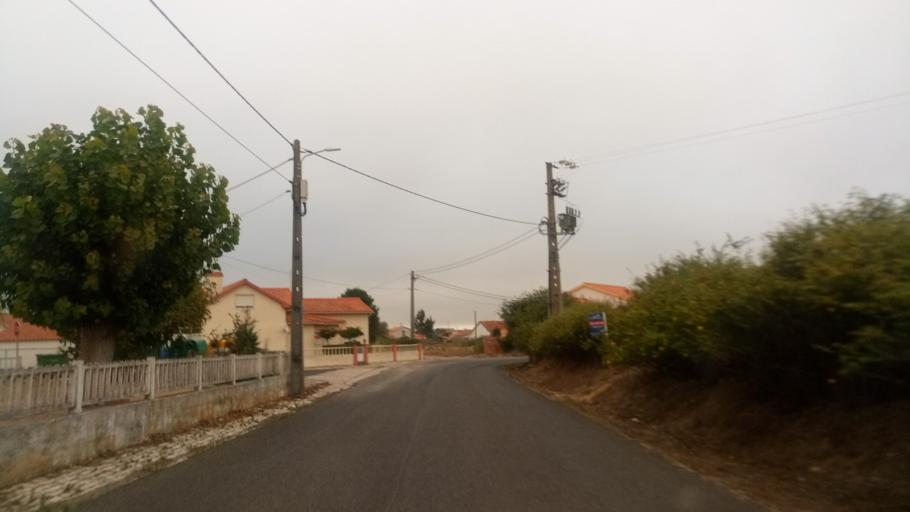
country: PT
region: Leiria
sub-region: Caldas da Rainha
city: Caldas da Rainha
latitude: 39.4534
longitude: -9.1801
